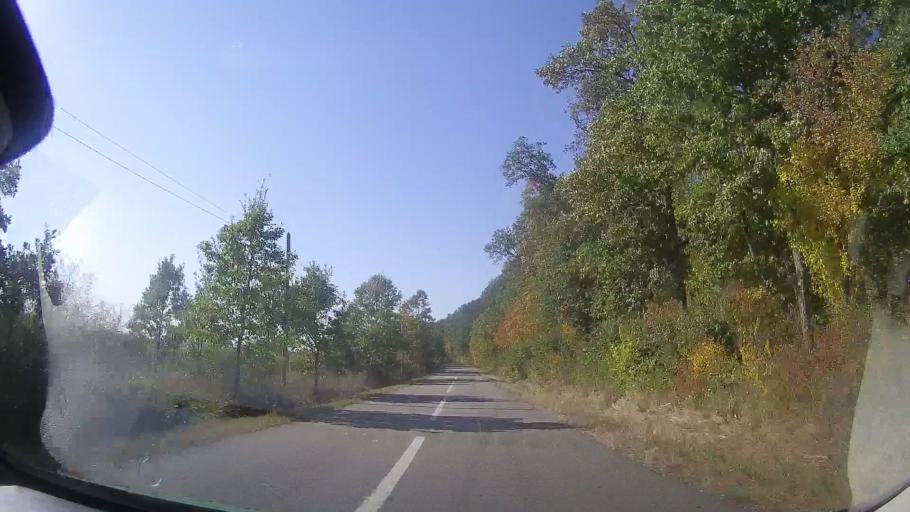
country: RO
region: Timis
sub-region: Comuna Ghizela
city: Ghizela
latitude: 45.8356
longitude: 21.7746
